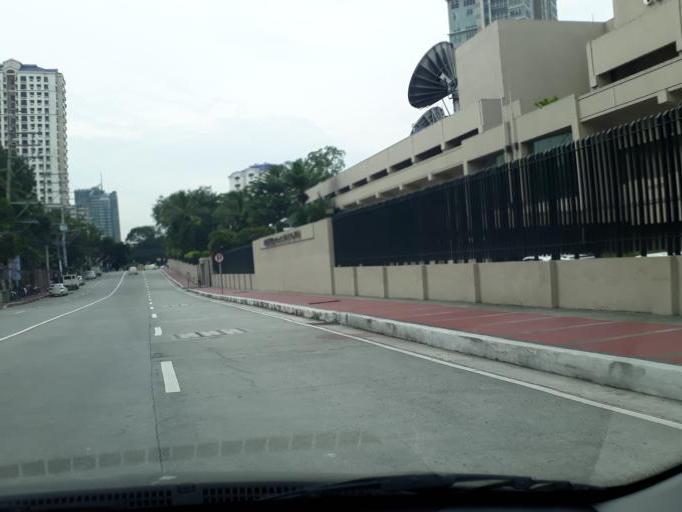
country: PH
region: Metro Manila
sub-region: Quezon City
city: Quezon City
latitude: 14.6403
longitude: 121.0372
